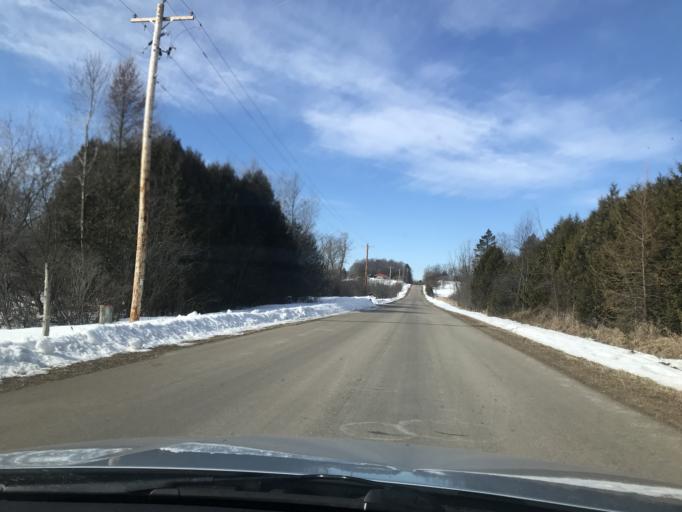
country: US
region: Wisconsin
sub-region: Oconto County
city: Gillett
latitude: 44.9618
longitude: -88.2939
